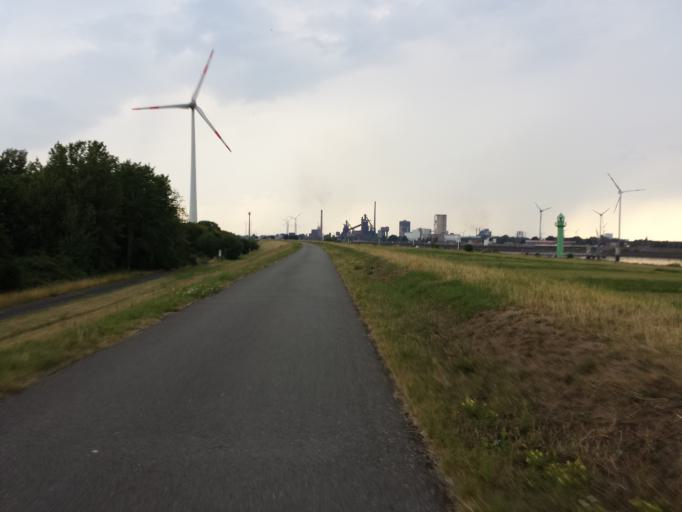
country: DE
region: Lower Saxony
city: Ritterhude
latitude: 53.1140
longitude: 8.7215
